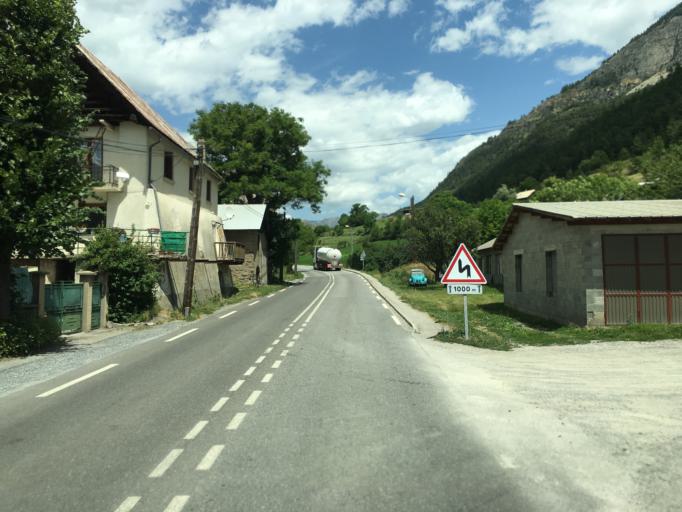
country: FR
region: Provence-Alpes-Cote d'Azur
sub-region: Departement des Hautes-Alpes
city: Saint-Martin-de-Queyrieres
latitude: 44.8241
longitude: 6.5796
